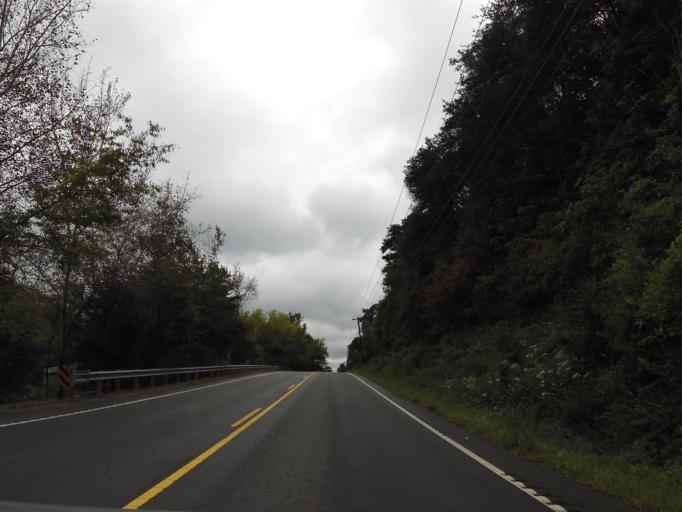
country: US
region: Tennessee
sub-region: Loudon County
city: Lenoir City
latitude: 35.7799
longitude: -84.2831
